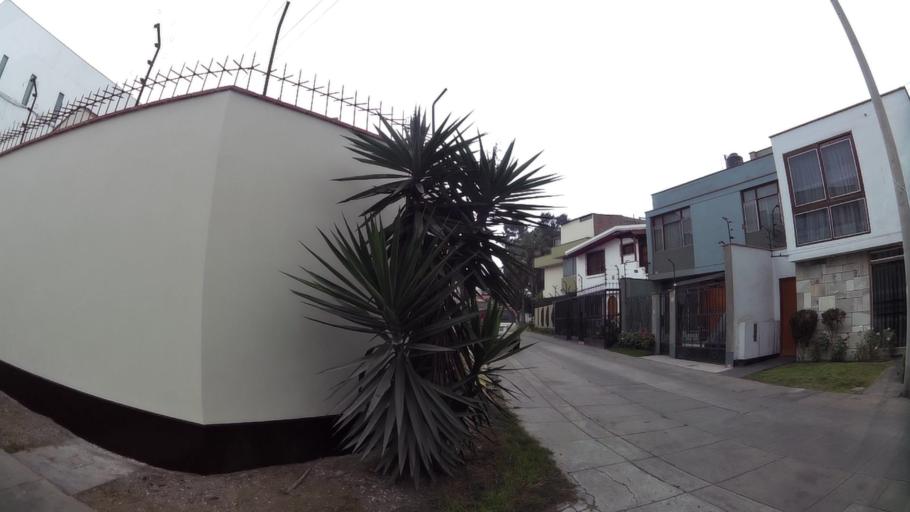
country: PE
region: Lima
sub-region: Lima
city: Surco
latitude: -12.1233
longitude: -76.9875
